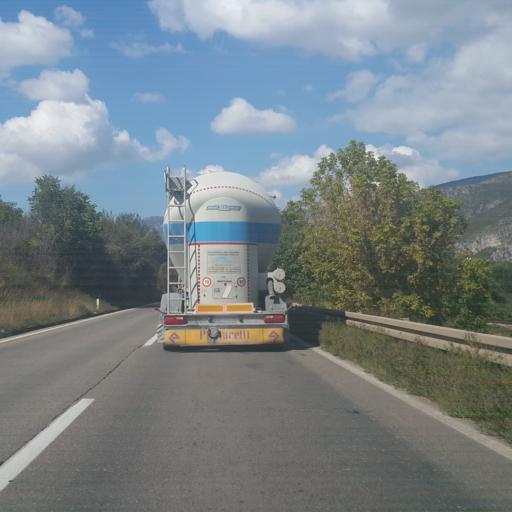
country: RS
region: Central Serbia
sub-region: Pirotski Okrug
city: Bela Palanka
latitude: 43.2819
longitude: 22.2220
